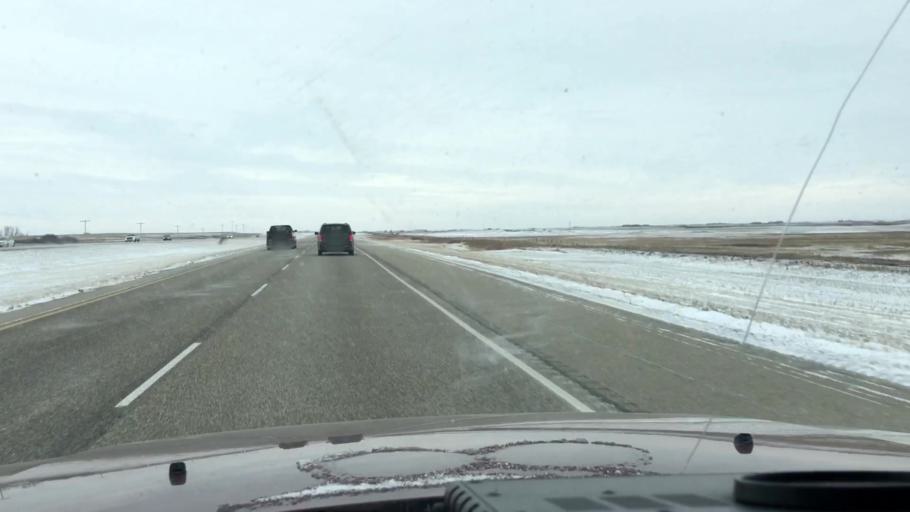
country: CA
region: Saskatchewan
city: Saskatoon
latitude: 51.5973
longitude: -106.3914
